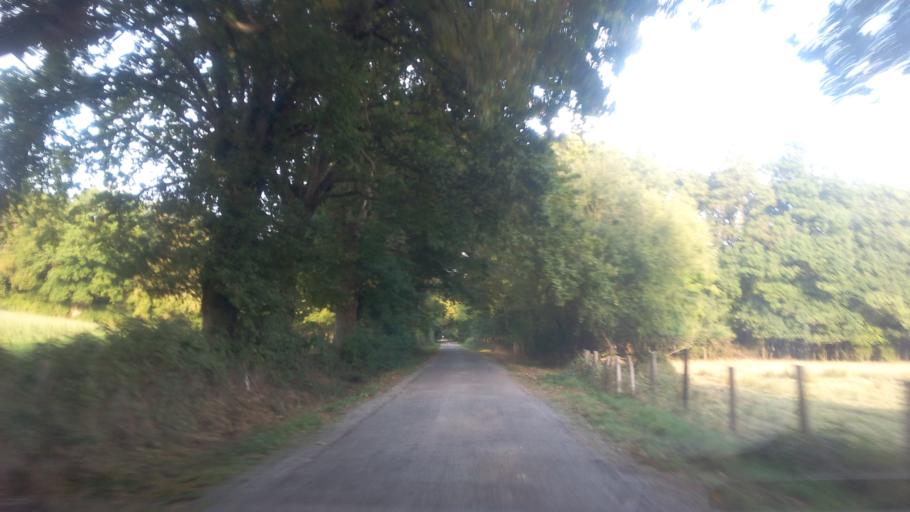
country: FR
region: Pays de la Loire
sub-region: Departement de la Loire-Atlantique
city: Saint-Nicolas-de-Redon
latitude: 47.6569
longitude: -2.0546
